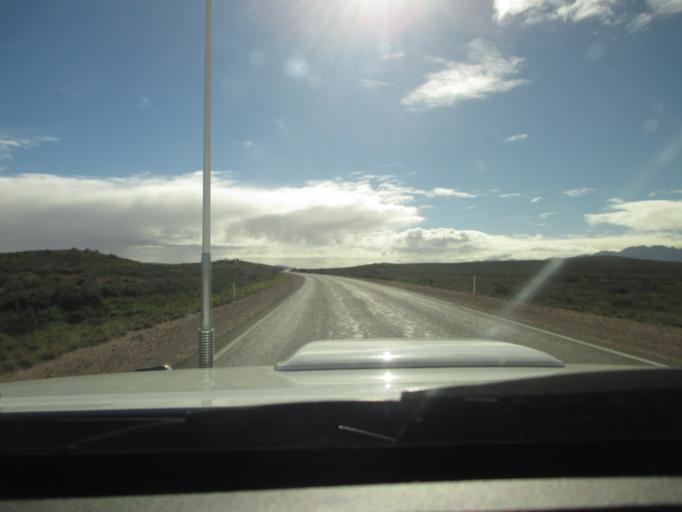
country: AU
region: South Australia
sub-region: Flinders Ranges
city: Quorn
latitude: -31.7489
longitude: 138.3366
